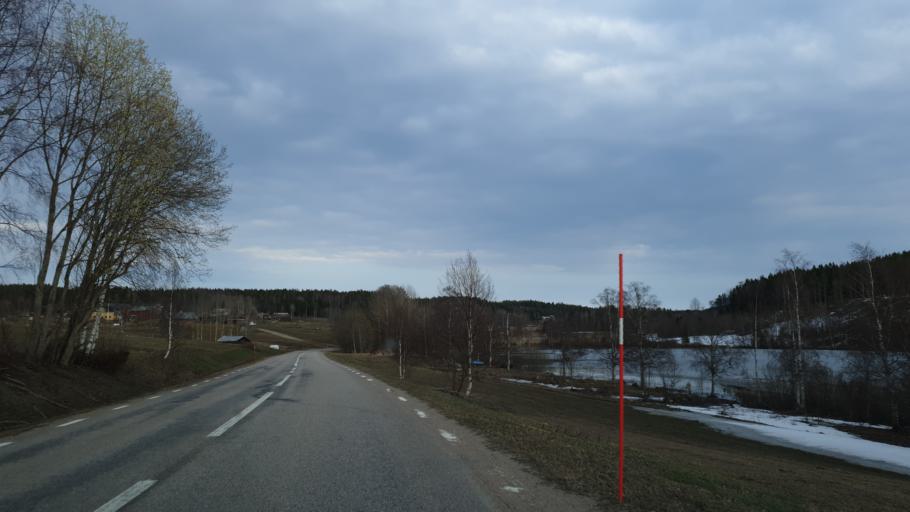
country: SE
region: Gaevleborg
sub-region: Nordanstigs Kommun
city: Bergsjoe
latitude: 61.9793
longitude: 17.2783
